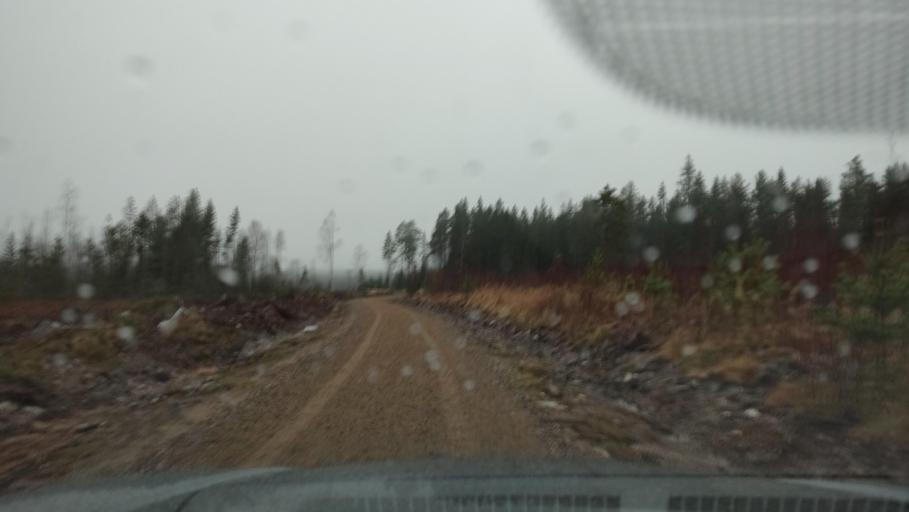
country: FI
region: Southern Ostrobothnia
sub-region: Suupohja
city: Karijoki
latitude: 62.1992
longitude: 21.7751
